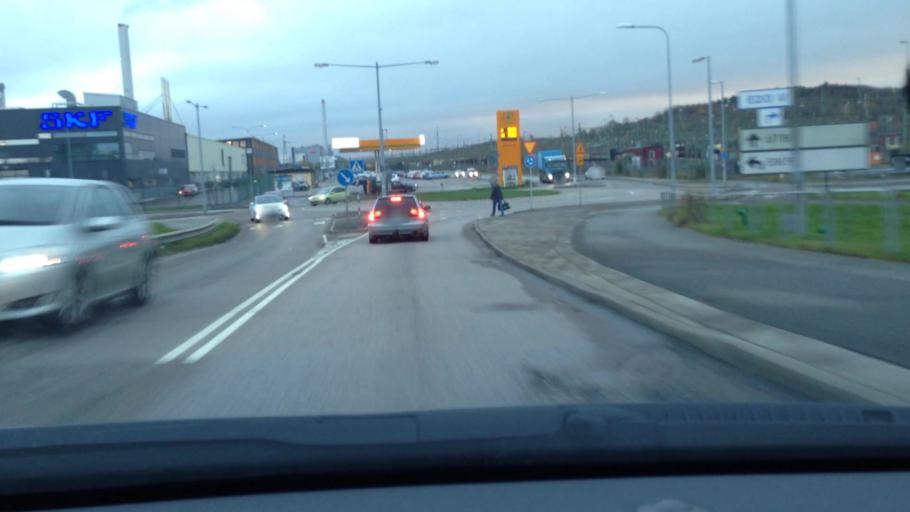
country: SE
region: Vaestra Goetaland
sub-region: Goteborg
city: Eriksbo
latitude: 57.7270
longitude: 12.0254
